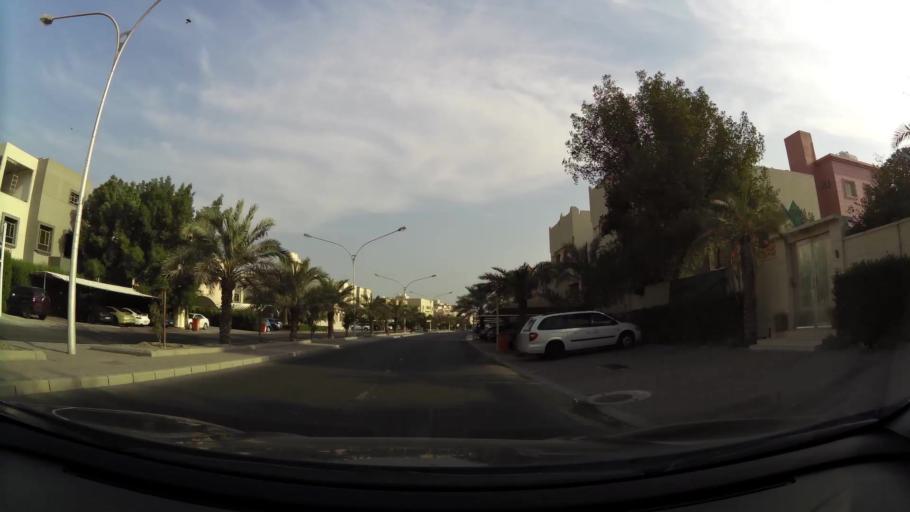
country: KW
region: Muhafazat Hawalli
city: Hawalli
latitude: 29.3115
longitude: 48.0134
